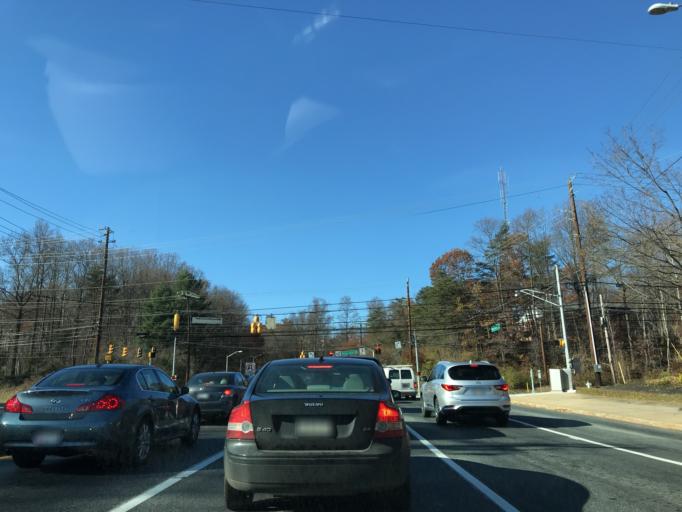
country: US
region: Maryland
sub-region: Montgomery County
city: Rockville
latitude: 39.0570
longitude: -77.1607
